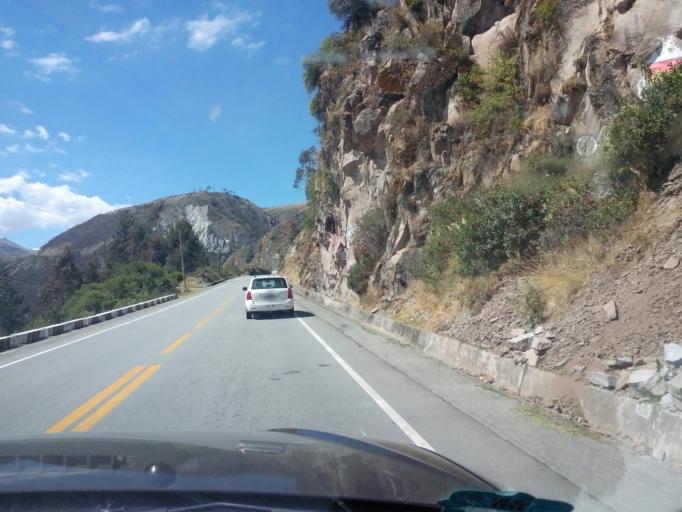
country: PE
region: Cusco
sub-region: Provincia de Anta
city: Ancahuasi
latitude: -13.4462
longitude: -72.3795
